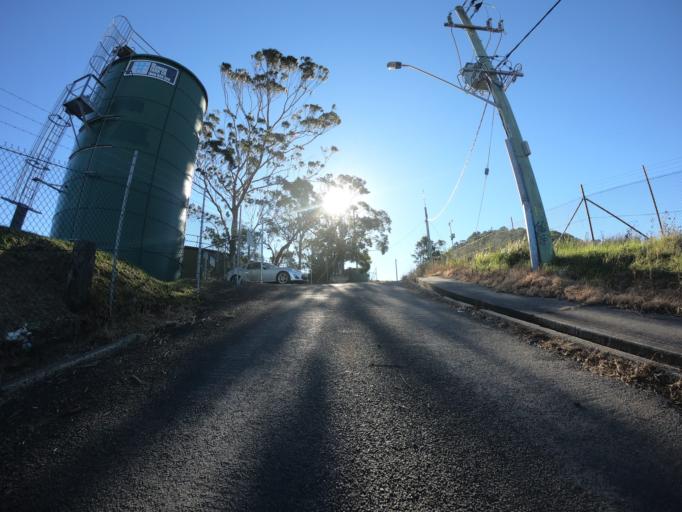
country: AU
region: New South Wales
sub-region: Wollongong
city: Mount Keira
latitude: -34.4224
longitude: 150.8404
